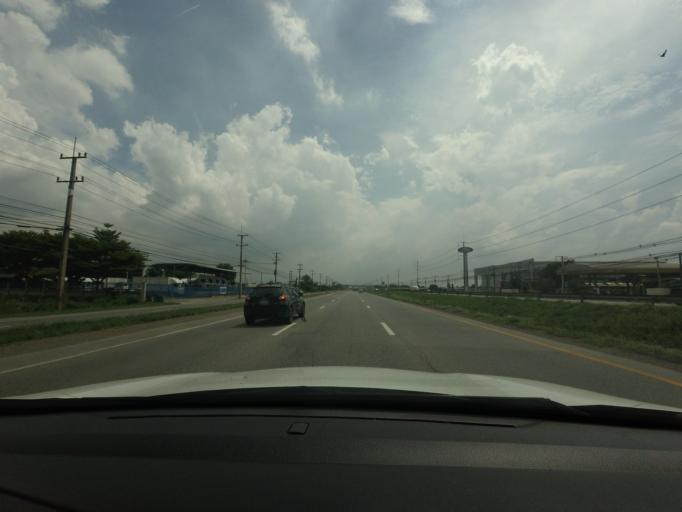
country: TH
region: Phra Nakhon Si Ayutthaya
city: Wang Noi
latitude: 14.2100
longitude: 100.6755
